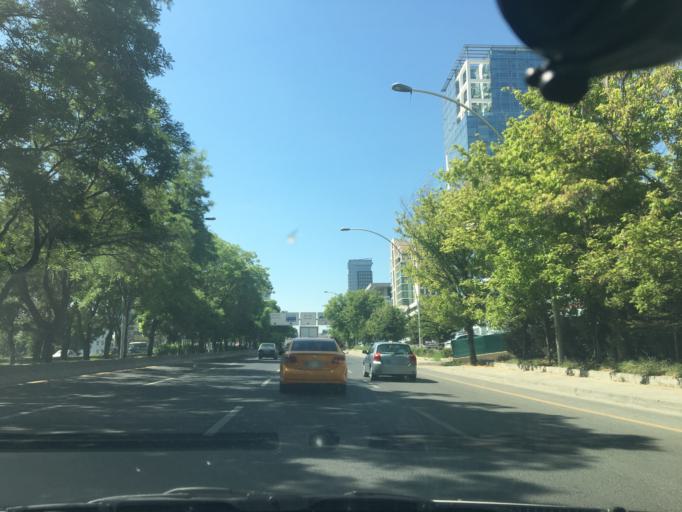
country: TR
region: Ankara
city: Ankara
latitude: 39.8926
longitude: 32.8129
